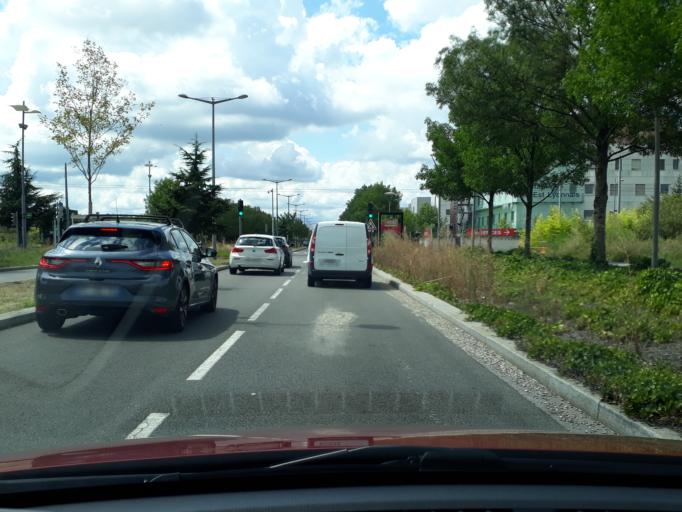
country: FR
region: Rhone-Alpes
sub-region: Departement du Rhone
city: Bron
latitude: 45.7173
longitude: 4.9286
